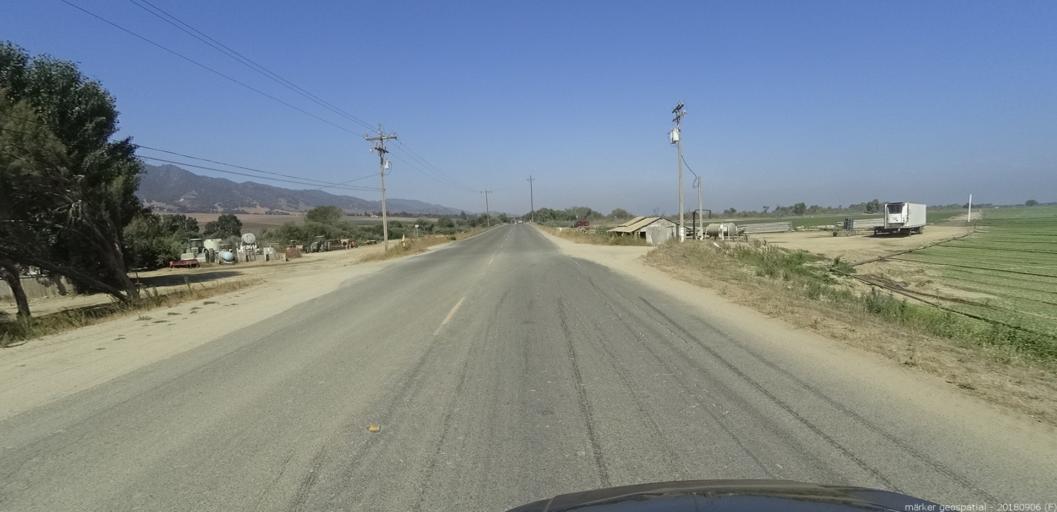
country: US
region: California
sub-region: Monterey County
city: Chualar
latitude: 36.5539
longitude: -121.5441
